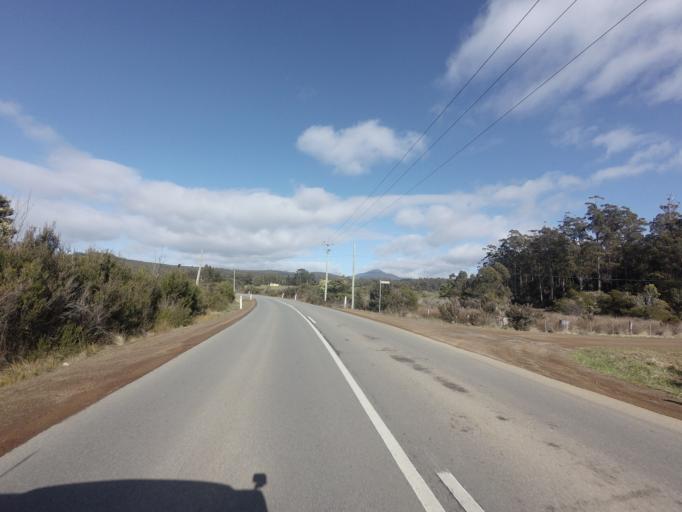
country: AU
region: Tasmania
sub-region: Huon Valley
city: Geeveston
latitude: -43.3261
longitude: 146.9726
